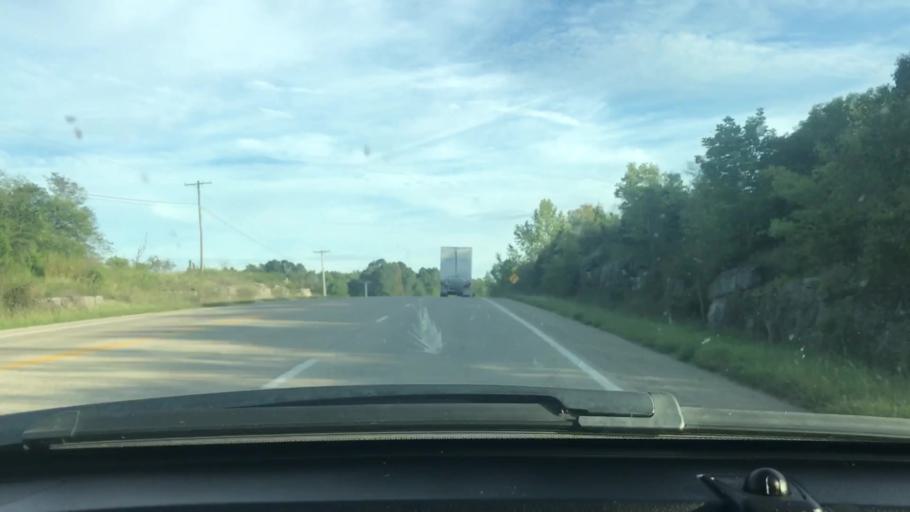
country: US
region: Arkansas
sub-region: Randolph County
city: Pocahontas
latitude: 36.1903
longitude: -91.1644
